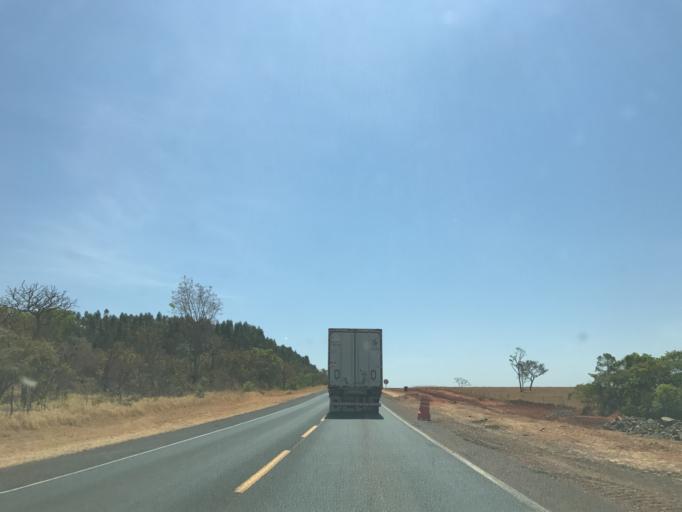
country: BR
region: Minas Gerais
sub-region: Prata
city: Prata
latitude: -19.4543
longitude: -48.8832
